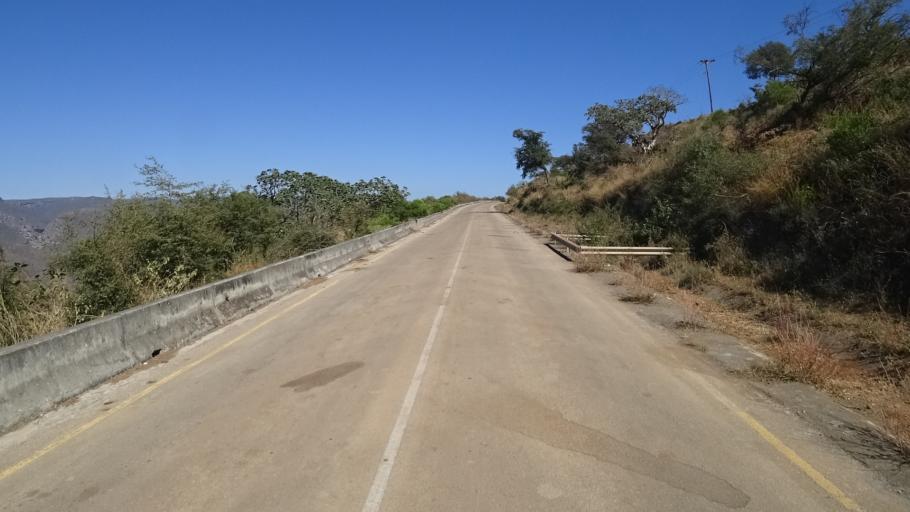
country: YE
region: Al Mahrah
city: Hawf
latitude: 16.7450
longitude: 53.3880
